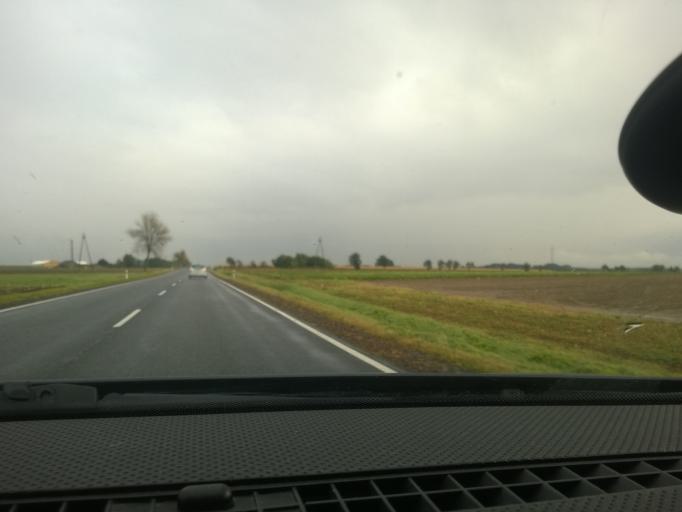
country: PL
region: Lodz Voivodeship
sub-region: Powiat sieradzki
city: Blaszki
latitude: 51.6821
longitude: 18.3385
